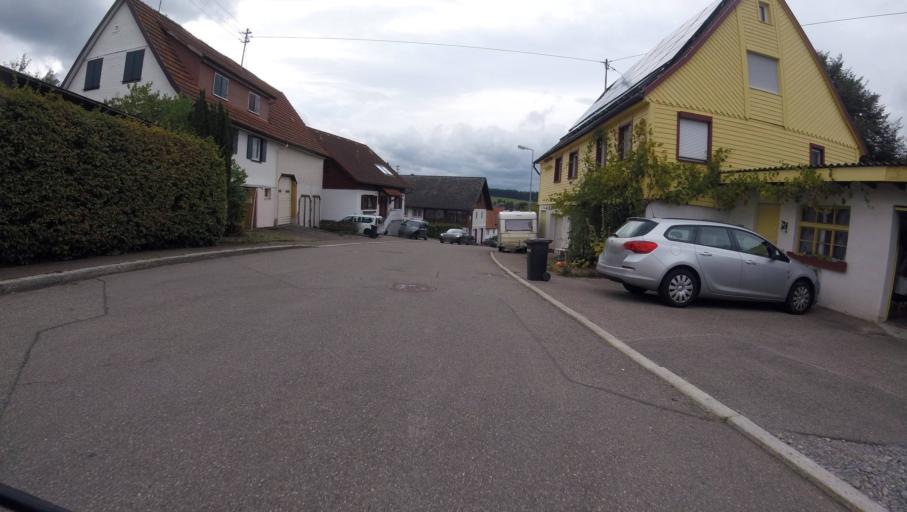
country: DE
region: Baden-Wuerttemberg
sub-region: Karlsruhe Region
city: Enzklosterle
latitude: 48.5970
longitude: 8.4264
